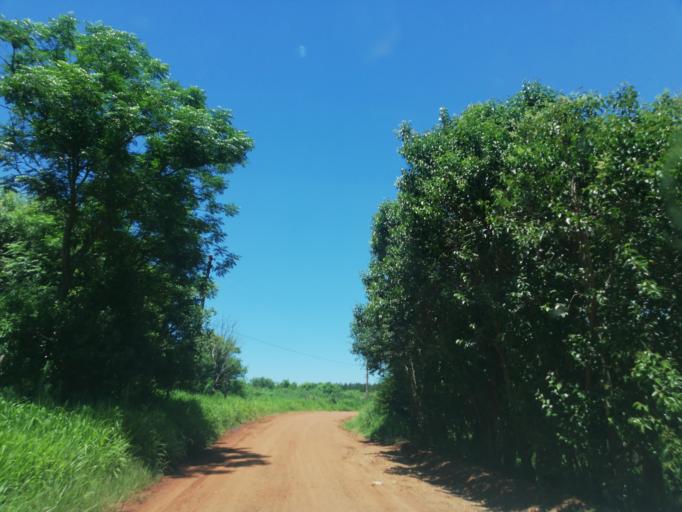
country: AR
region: Misiones
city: Garupa
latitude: -27.4511
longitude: -55.9042
